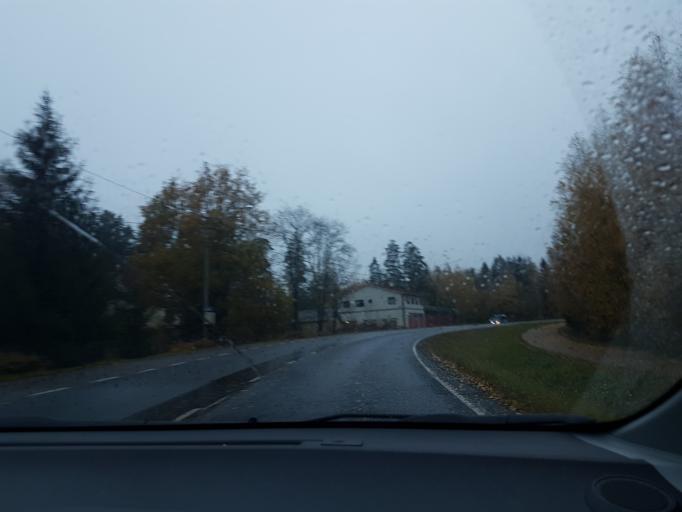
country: FI
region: Uusimaa
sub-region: Helsinki
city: Jaervenpaeae
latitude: 60.5457
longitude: 25.1182
